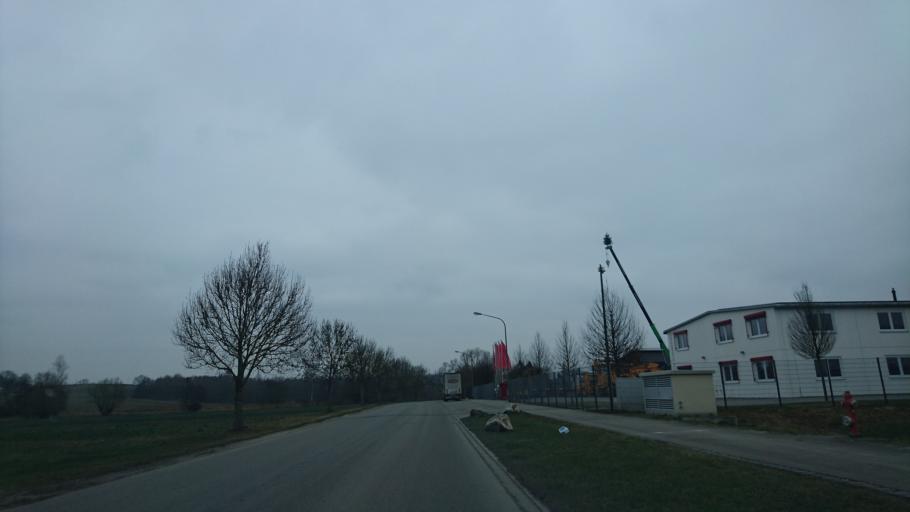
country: DE
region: Bavaria
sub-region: Swabia
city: Zusmarshausen
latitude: 48.4162
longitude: 10.5922
